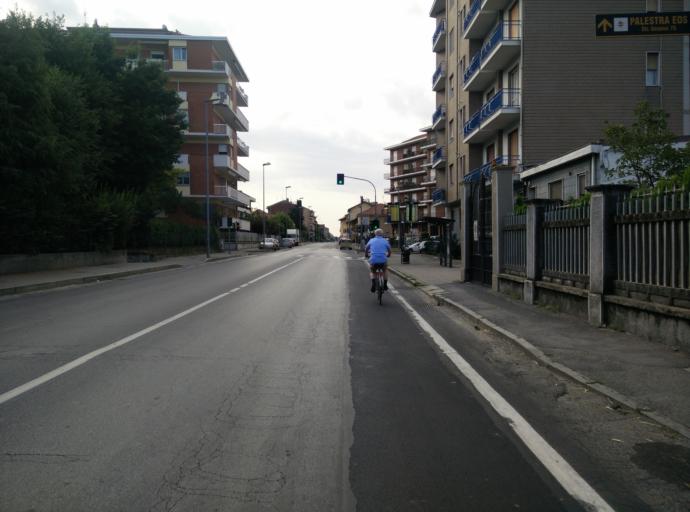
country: IT
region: Piedmont
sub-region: Provincia di Torino
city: Moncalieri
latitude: 44.9979
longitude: 7.7021
